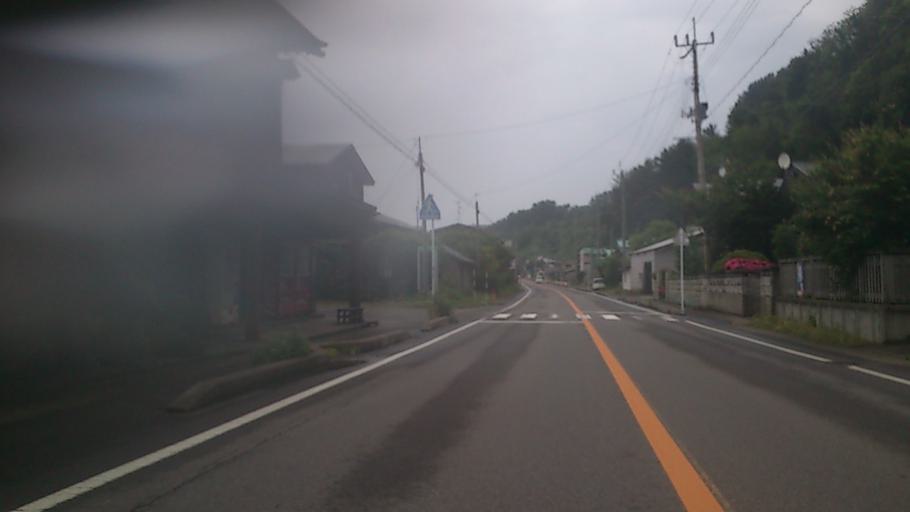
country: JP
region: Akita
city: Noshiromachi
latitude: 40.4917
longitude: 139.9504
